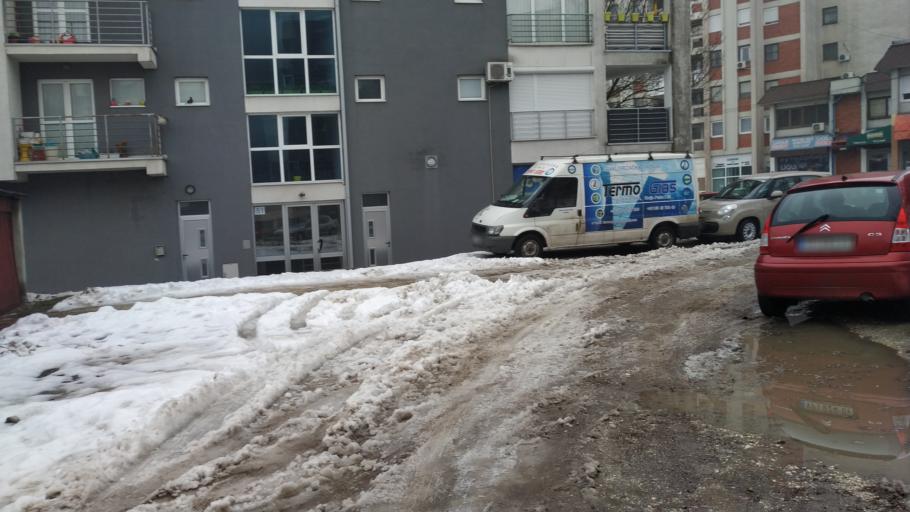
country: RS
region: Central Serbia
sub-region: Podunavski Okrug
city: Velika Plana
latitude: 44.3303
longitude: 21.0728
